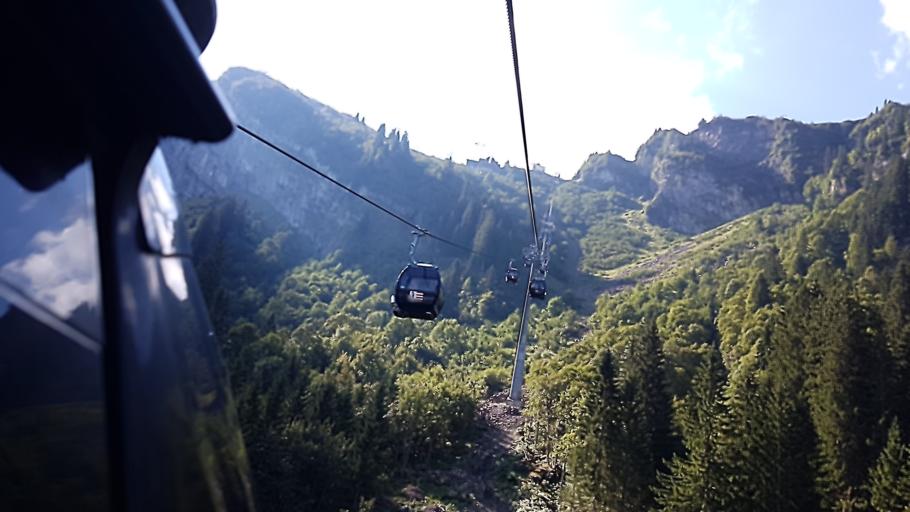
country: CH
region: Obwalden
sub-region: Obwalden
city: Engelberg
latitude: 46.8007
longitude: 8.3976
